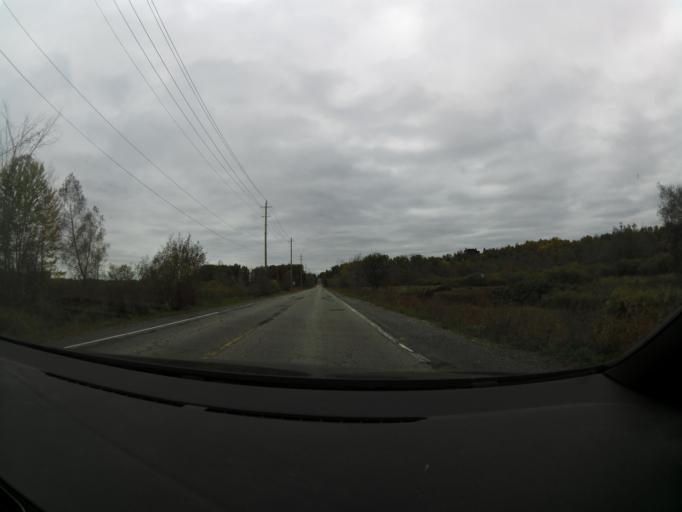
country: CA
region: Ontario
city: Bells Corners
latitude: 45.3240
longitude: -75.9641
